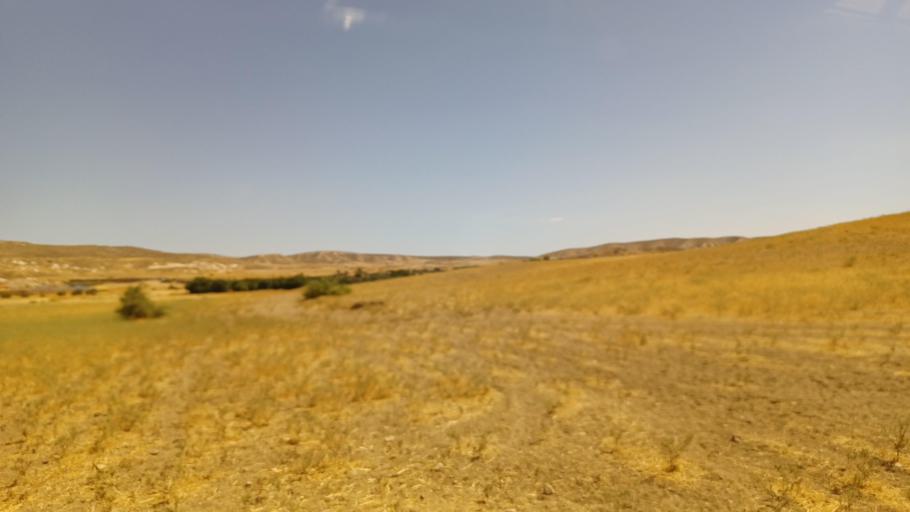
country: CY
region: Larnaka
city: Troulloi
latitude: 35.0246
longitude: 33.6003
